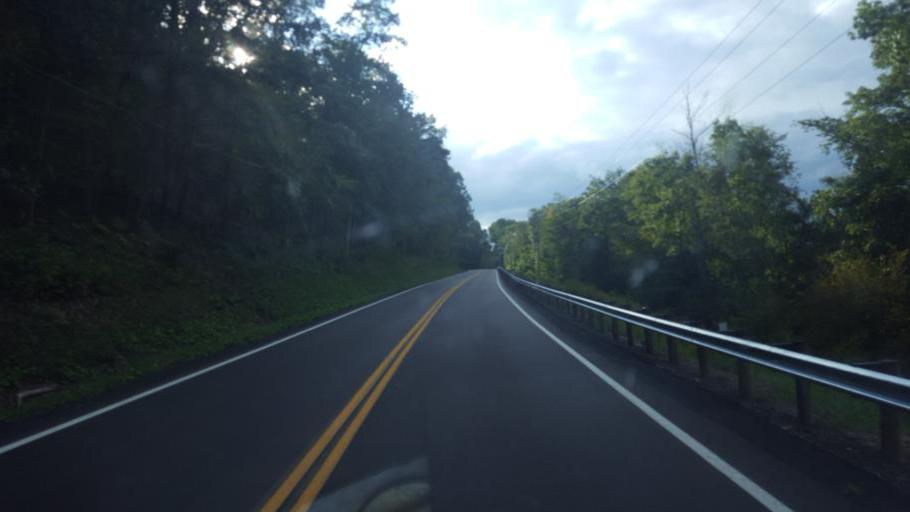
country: US
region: Ohio
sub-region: Knox County
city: Oak Hill
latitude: 40.4622
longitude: -82.1130
